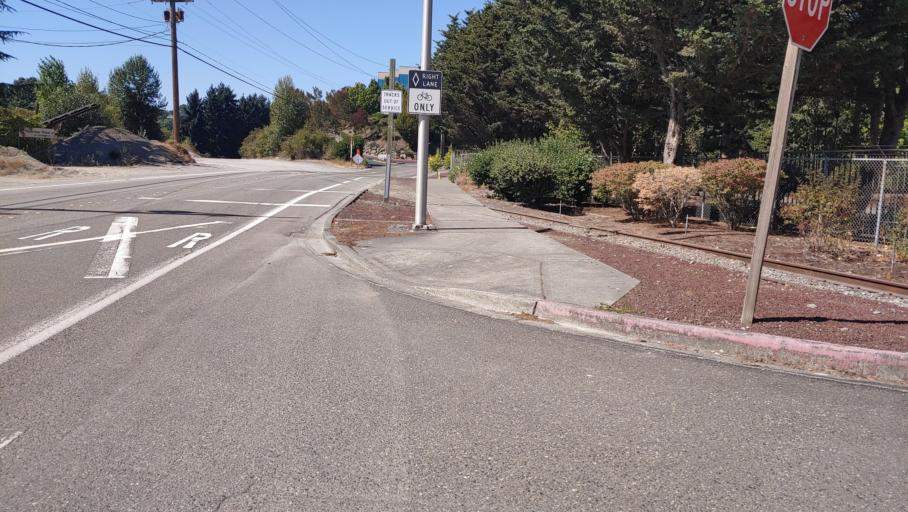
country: US
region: Washington
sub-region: King County
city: Tukwila
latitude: 47.4687
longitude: -122.2429
